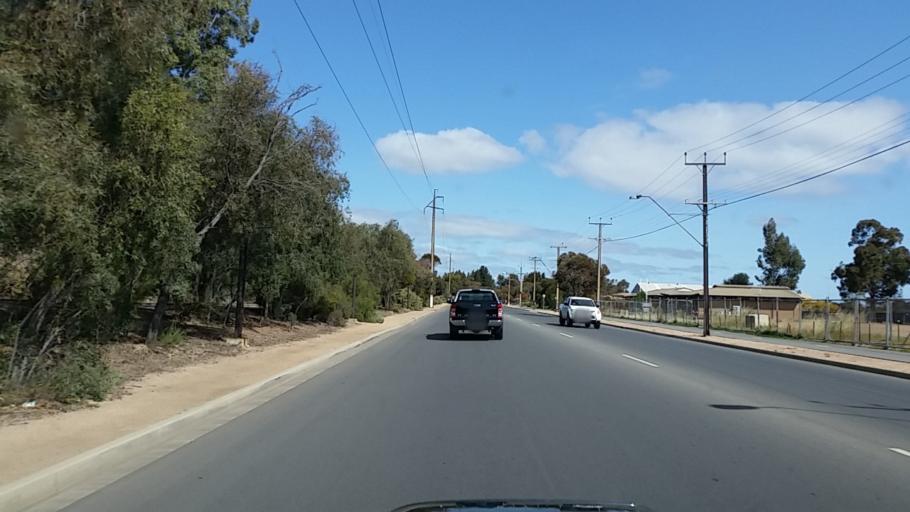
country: AU
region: South Australia
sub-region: Port Pirie City and Dists
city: Port Pirie
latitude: -33.1850
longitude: 138.0115
